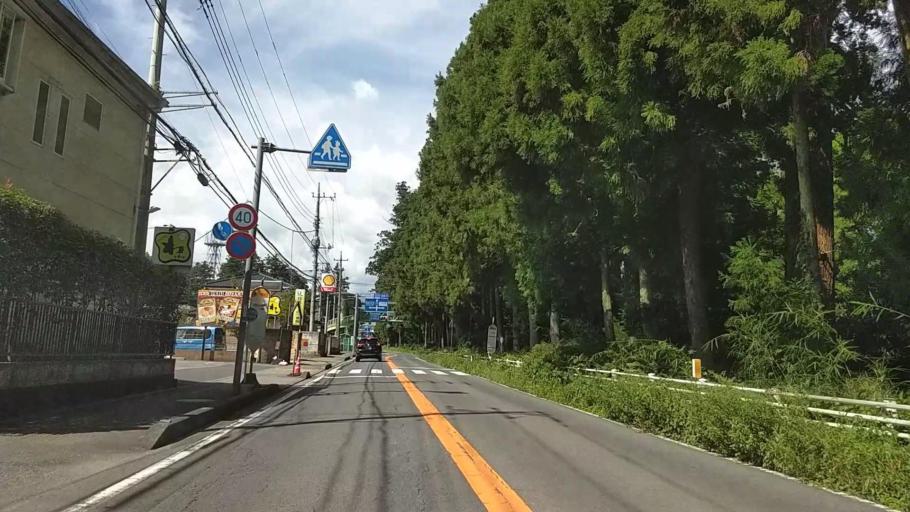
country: JP
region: Tochigi
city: Imaichi
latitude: 36.7219
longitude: 139.6945
